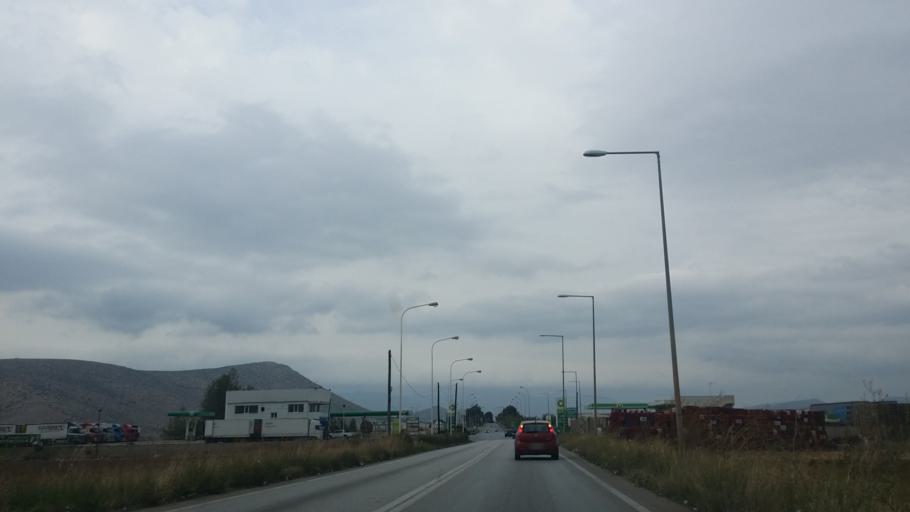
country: GR
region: Central Greece
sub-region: Nomos Voiotias
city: Thivai
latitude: 38.3584
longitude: 23.3220
